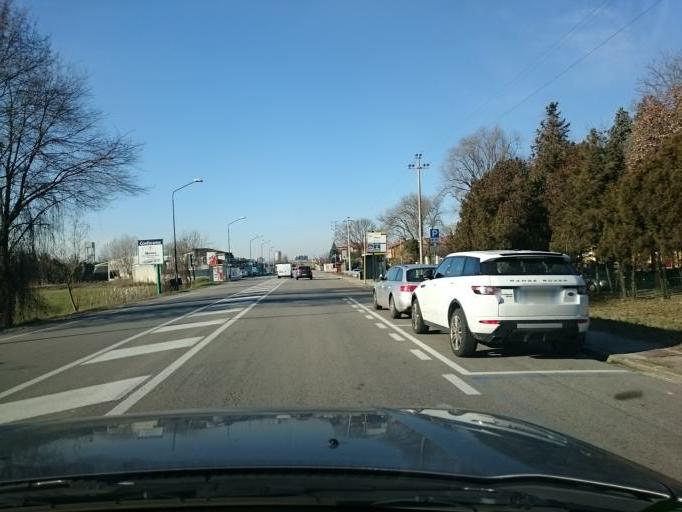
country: IT
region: Veneto
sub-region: Provincia di Venezia
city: Mestre
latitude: 45.4787
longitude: 12.2608
